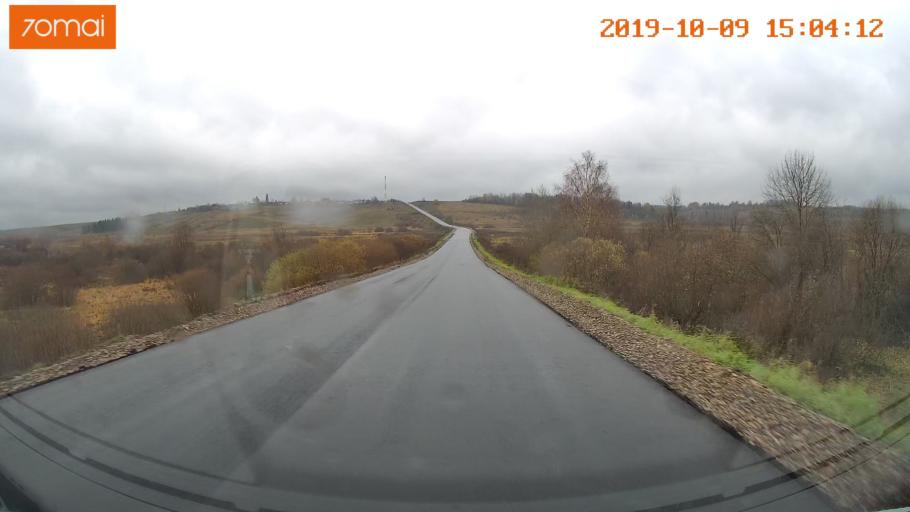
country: RU
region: Kostroma
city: Chistyye Bory
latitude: 58.2616
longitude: 41.6694
